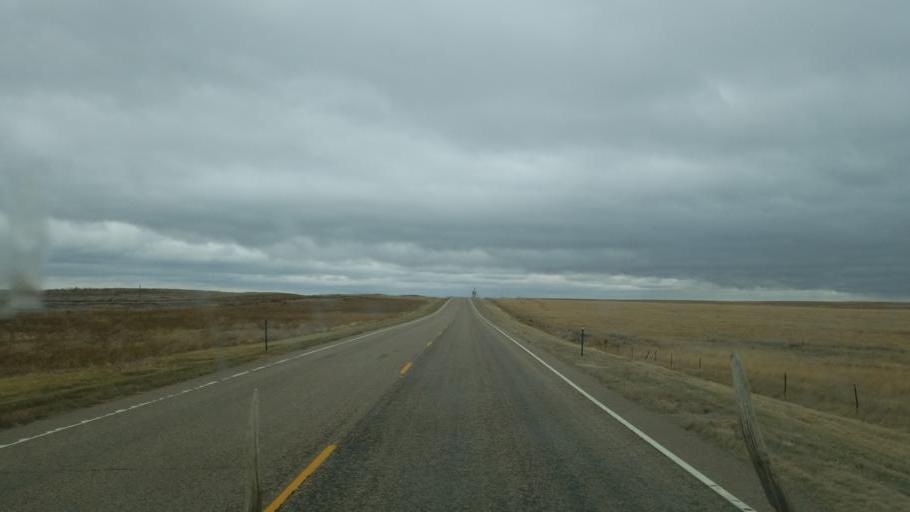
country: US
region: Colorado
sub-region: Cheyenne County
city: Cheyenne Wells
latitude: 38.8150
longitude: -102.5609
